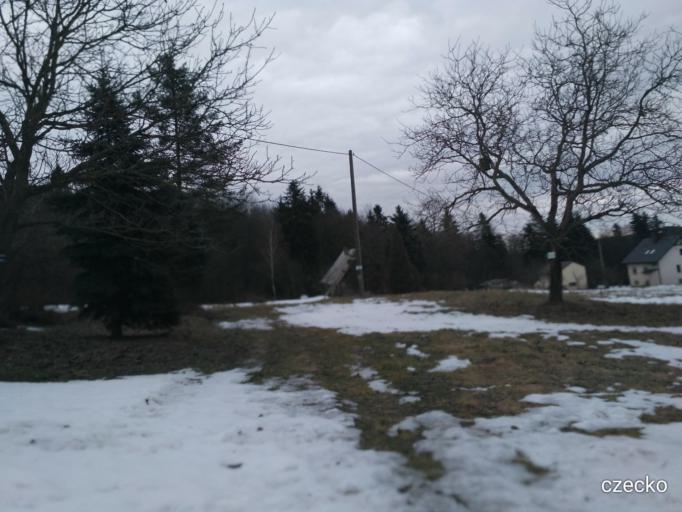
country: PL
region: Subcarpathian Voivodeship
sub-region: Powiat krosnienski
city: Korczyna
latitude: 49.7468
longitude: 21.8248
